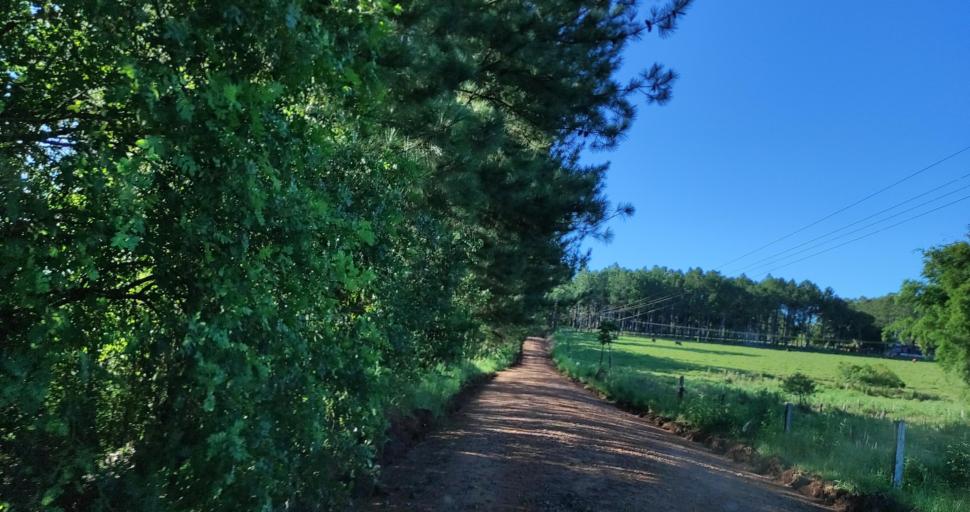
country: AR
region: Misiones
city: Puerto Rico
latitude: -26.8351
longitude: -55.0019
